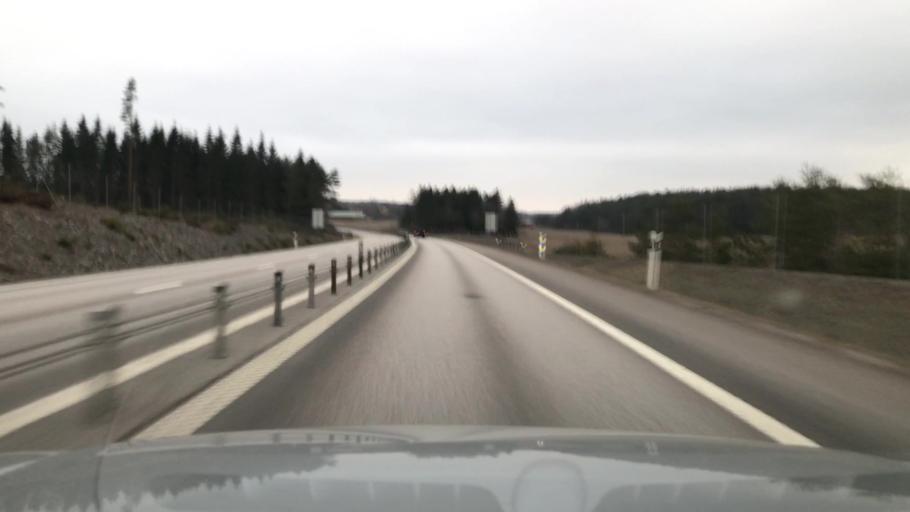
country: SE
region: OEstergoetland
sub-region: Valdemarsviks Kommun
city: Gusum
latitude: 58.3002
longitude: 16.4933
